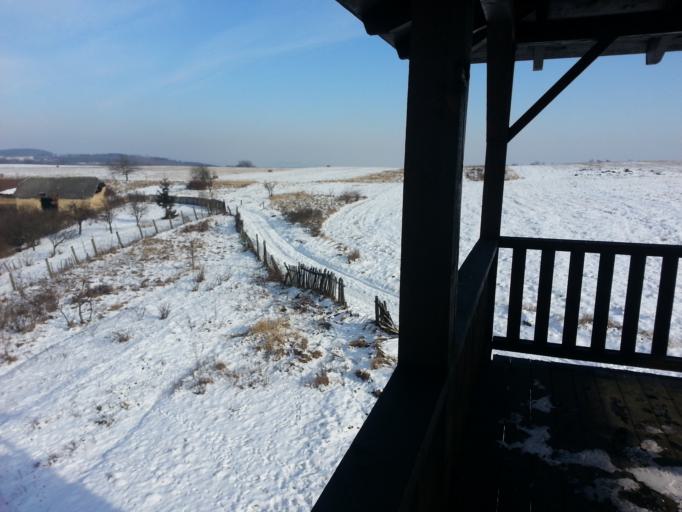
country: HU
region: Nograd
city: Somoskoujfalu
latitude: 48.1276
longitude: 19.8844
